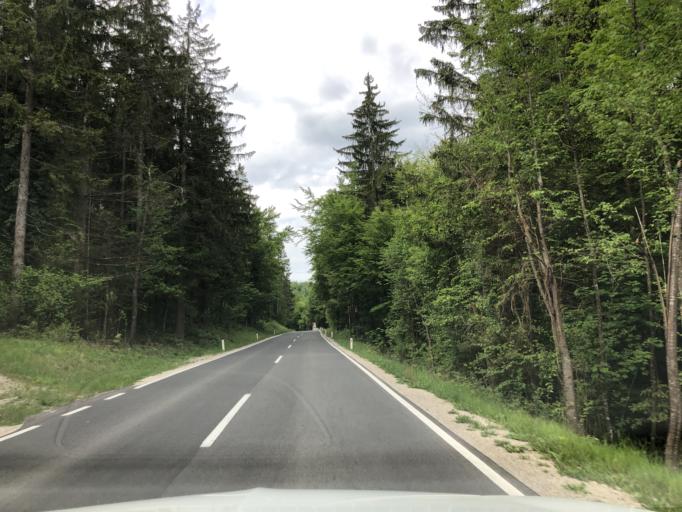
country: SI
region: Bloke
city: Nova Vas
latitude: 45.7554
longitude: 14.4686
